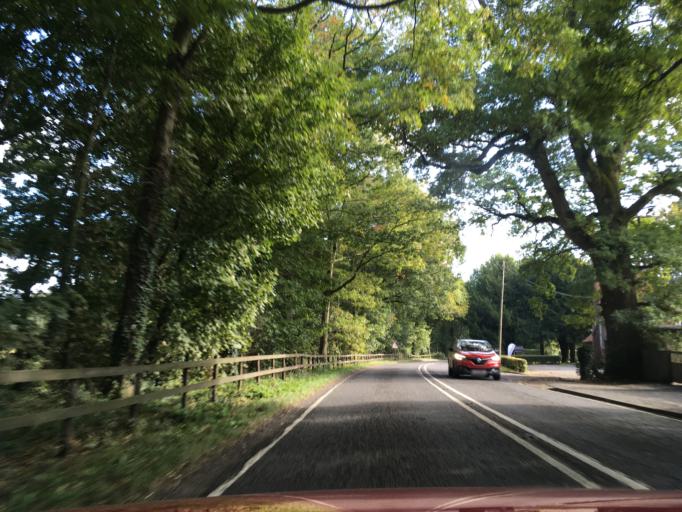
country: GB
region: England
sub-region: Hampshire
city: Old Basing
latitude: 51.2066
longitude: -1.0475
